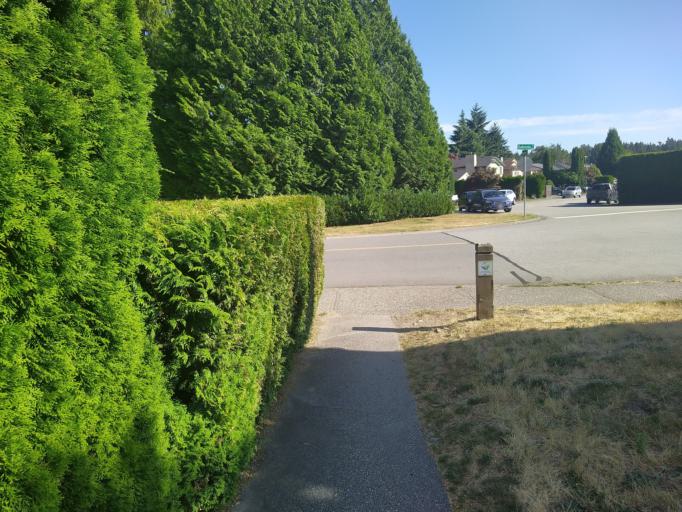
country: CA
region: British Columbia
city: Coquitlam
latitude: 49.2930
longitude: -122.7786
